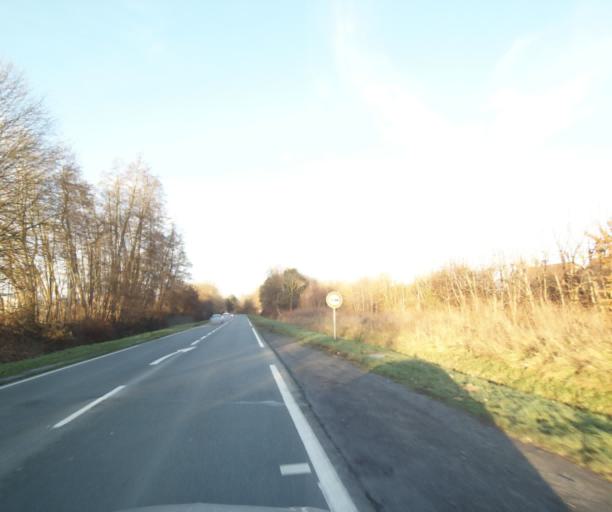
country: FR
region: Nord-Pas-de-Calais
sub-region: Departement du Nord
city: Famars
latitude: 50.3239
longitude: 3.5168
